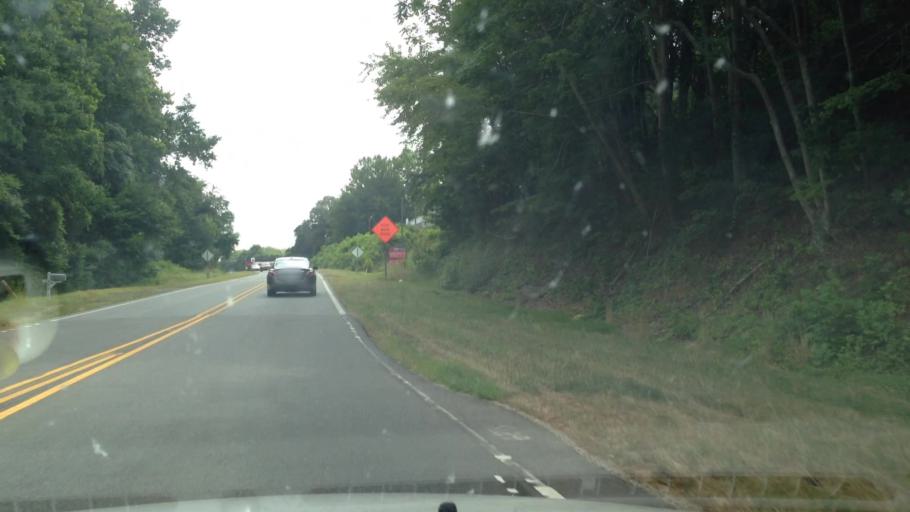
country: US
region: North Carolina
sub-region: Rockingham County
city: Reidsville
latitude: 36.3814
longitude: -79.6581
